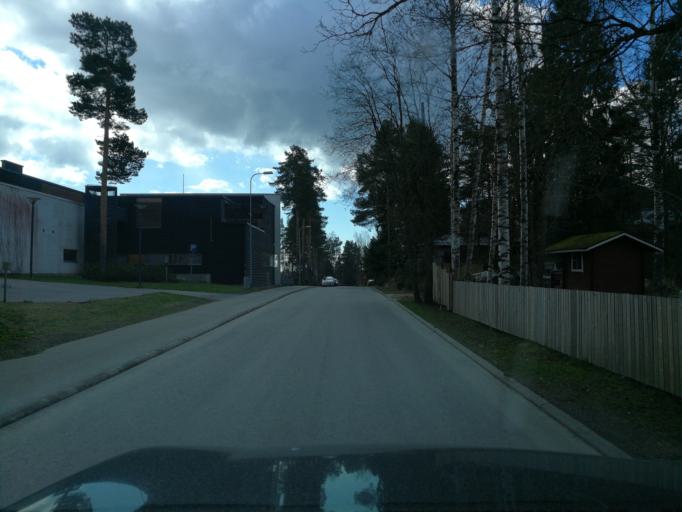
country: FI
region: Uusimaa
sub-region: Helsinki
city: Espoo
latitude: 60.1656
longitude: 24.6899
